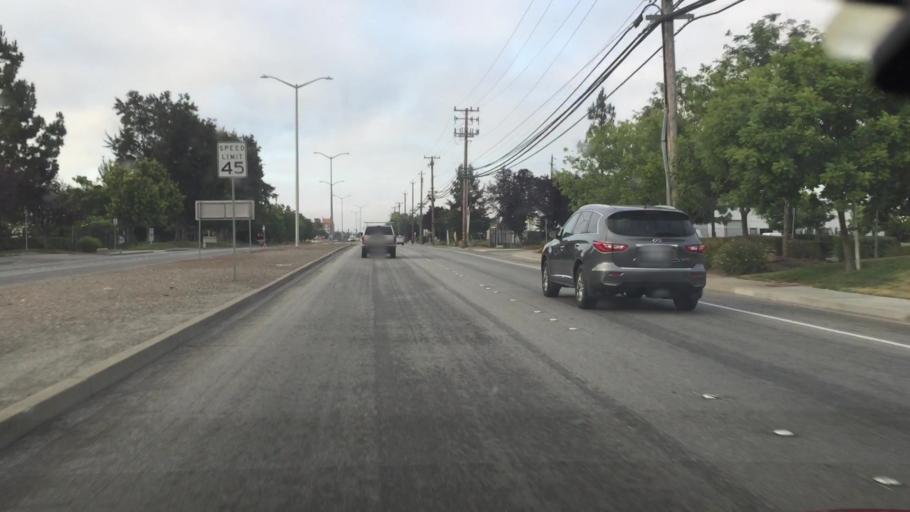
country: US
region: California
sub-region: Alameda County
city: Fremont
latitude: 37.5075
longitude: -121.9495
